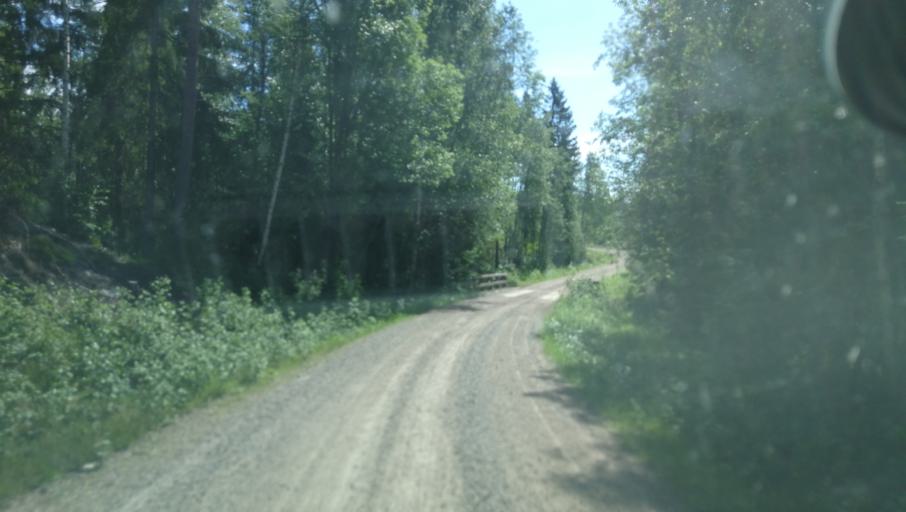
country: SE
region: Dalarna
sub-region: Vansbro Kommun
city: Vansbro
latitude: 60.8345
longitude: 14.1551
